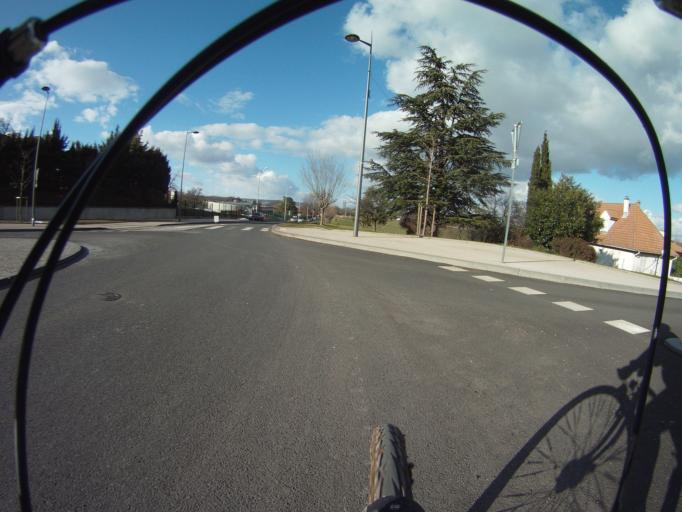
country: FR
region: Auvergne
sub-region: Departement du Puy-de-Dome
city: Perignat-les-Sarlieve
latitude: 45.7400
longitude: 3.1403
